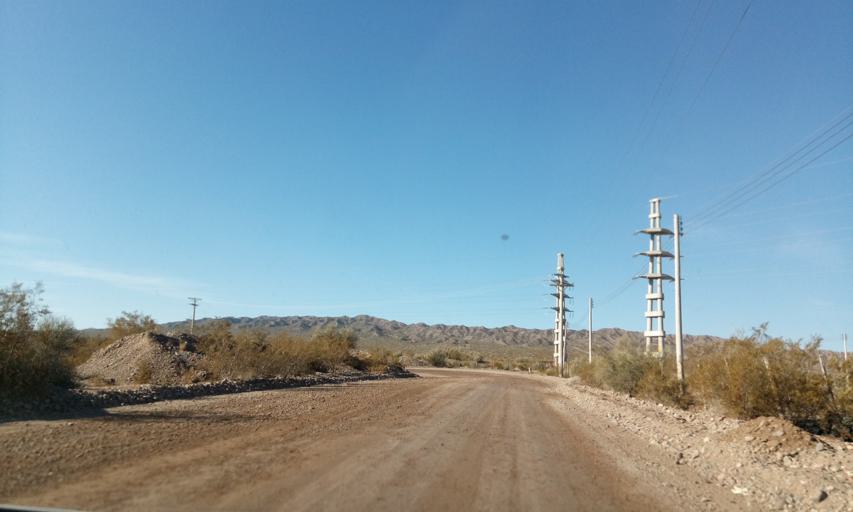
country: AR
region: San Juan
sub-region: Departamento de Rivadavia
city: Rivadavia
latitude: -31.4239
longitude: -68.6689
